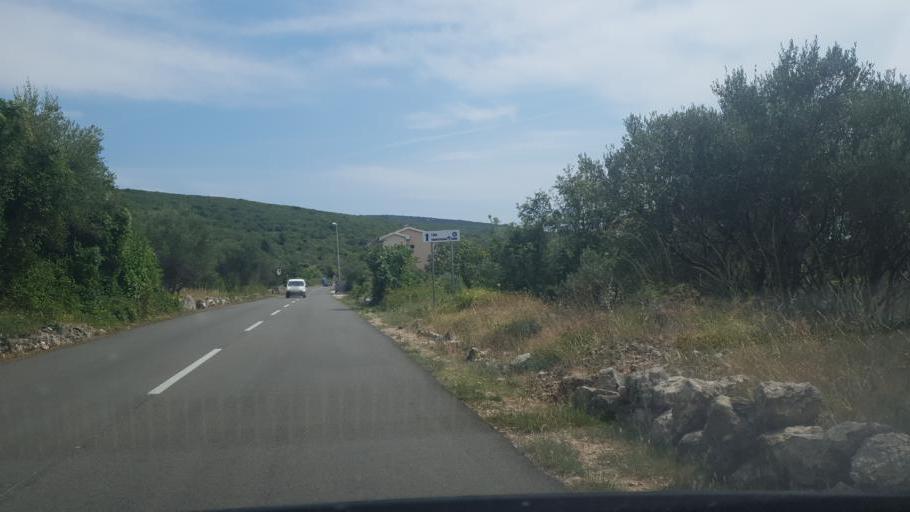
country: HR
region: Primorsko-Goranska
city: Punat
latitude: 45.0213
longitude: 14.6353
